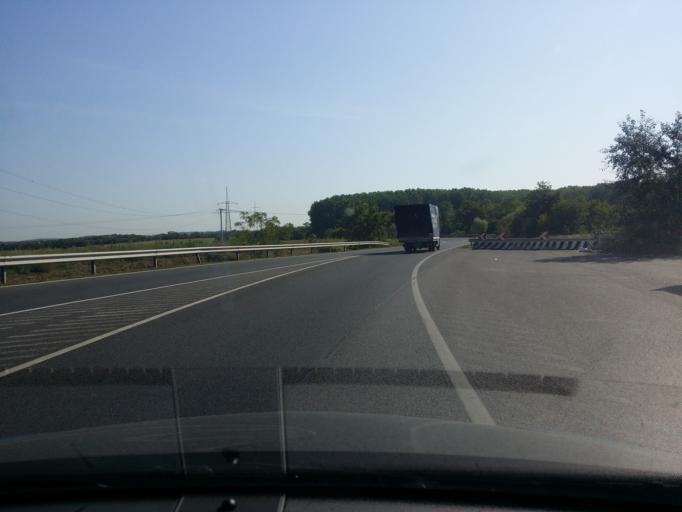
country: HU
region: Budapest
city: Budapest XVI. keruelet
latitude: 47.5439
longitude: 19.1715
